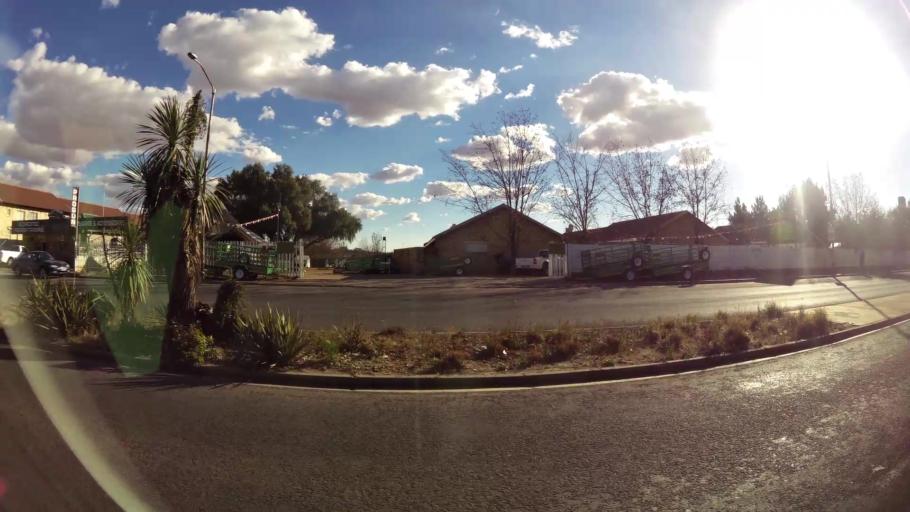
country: ZA
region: North-West
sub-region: Dr Kenneth Kaunda District Municipality
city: Klerksdorp
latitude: -26.8527
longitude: 26.6643
